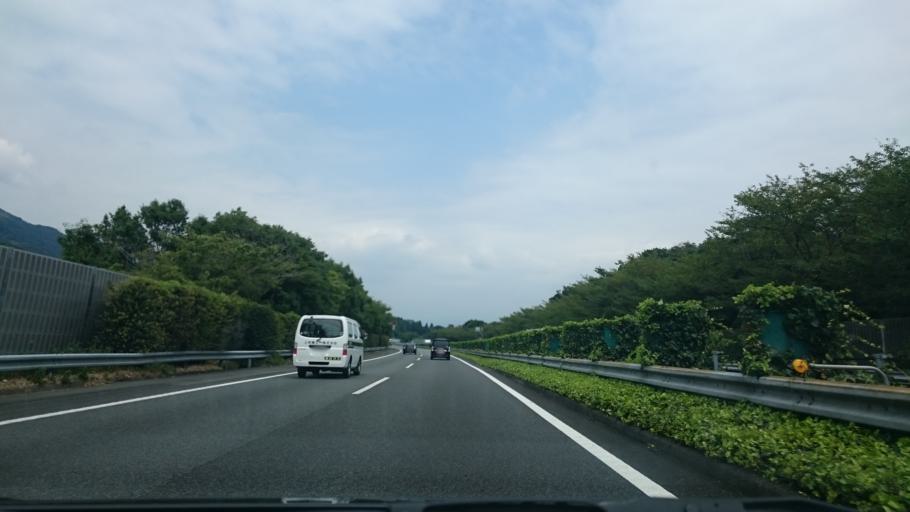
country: JP
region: Shizuoka
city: Fuji
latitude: 35.1328
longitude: 138.6144
